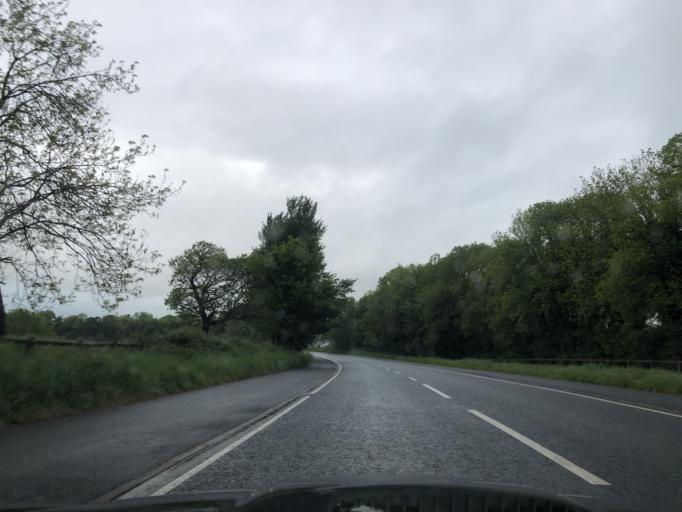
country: GB
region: Northern Ireland
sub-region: Antrim Borough
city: Antrim
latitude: 54.6982
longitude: -6.2243
